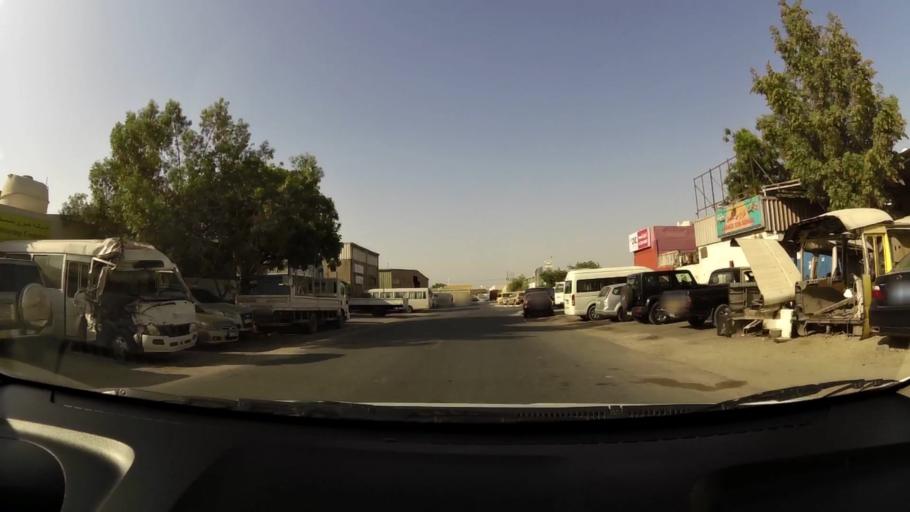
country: AE
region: Ash Shariqah
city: Sharjah
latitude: 25.2938
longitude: 55.3890
